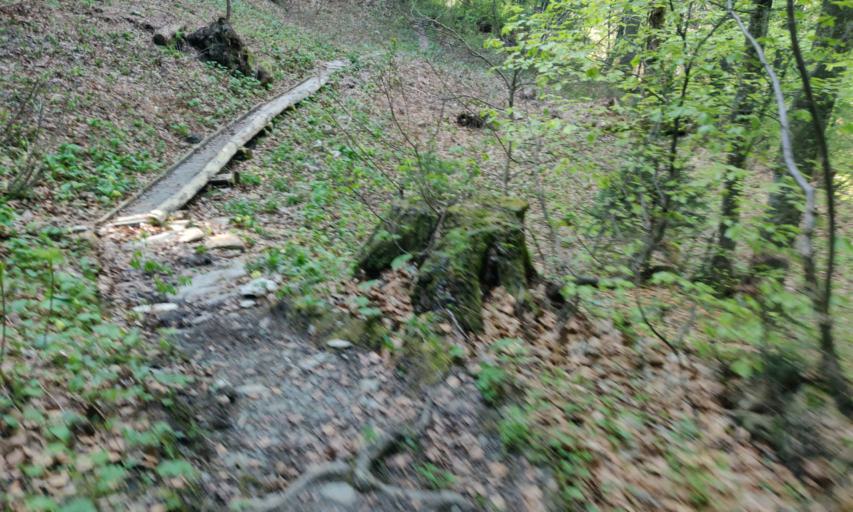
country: CH
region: Saint Gallen
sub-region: Wahlkreis Sarganserland
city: Sargans
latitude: 47.0742
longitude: 9.4418
